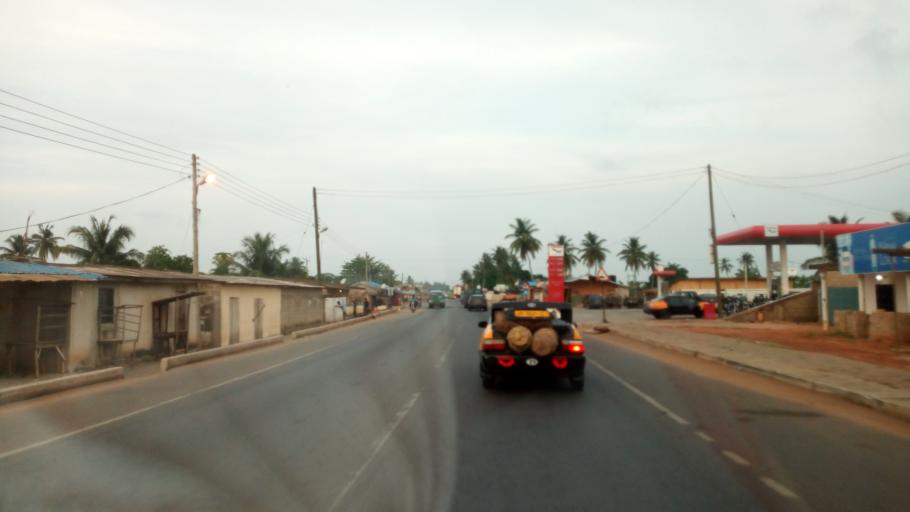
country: TG
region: Maritime
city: Lome
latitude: 6.1178
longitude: 1.1750
